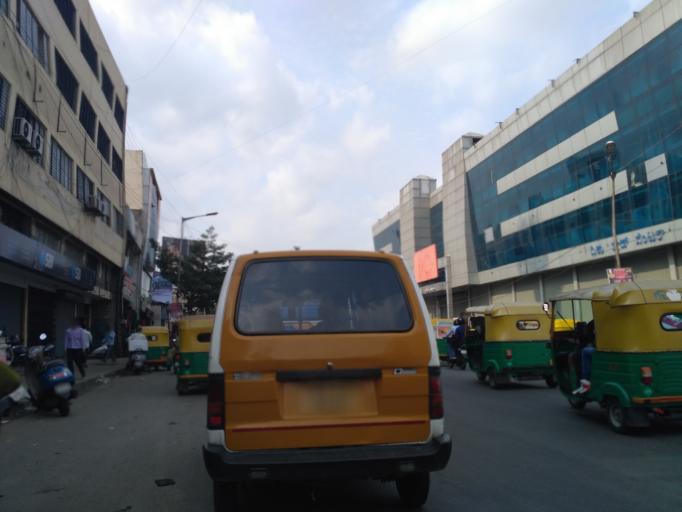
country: IN
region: Karnataka
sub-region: Bangalore Urban
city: Bangalore
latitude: 12.9605
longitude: 77.5836
